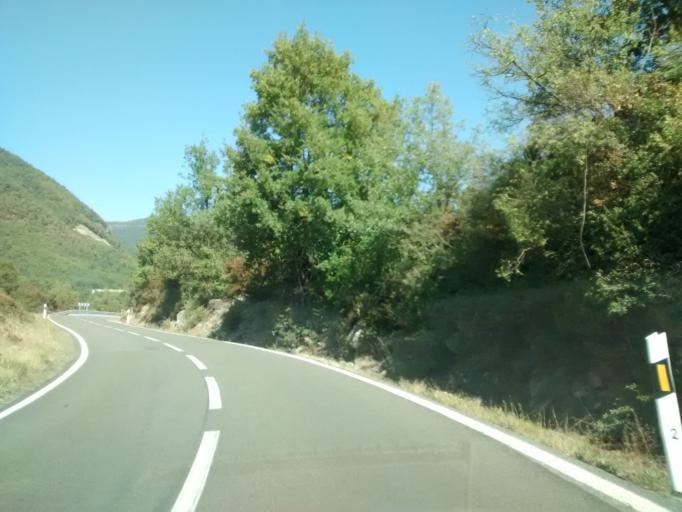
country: ES
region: Aragon
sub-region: Provincia de Huesca
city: Fiscal
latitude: 42.5107
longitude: -0.1258
